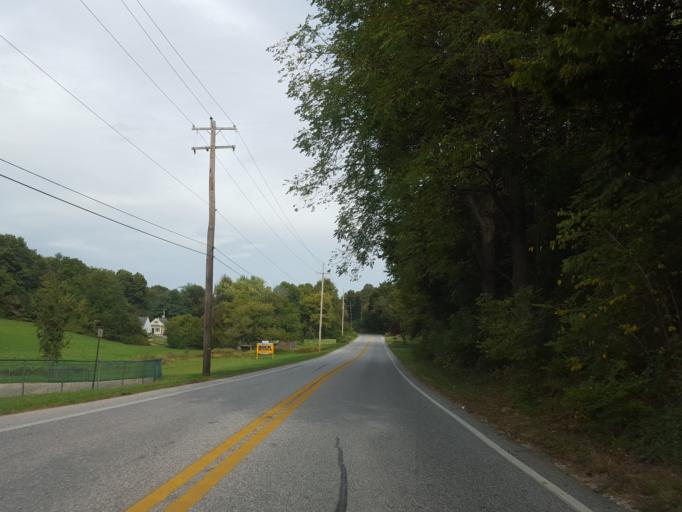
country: US
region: Pennsylvania
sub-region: York County
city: Yoe
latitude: 39.9056
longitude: -76.6281
